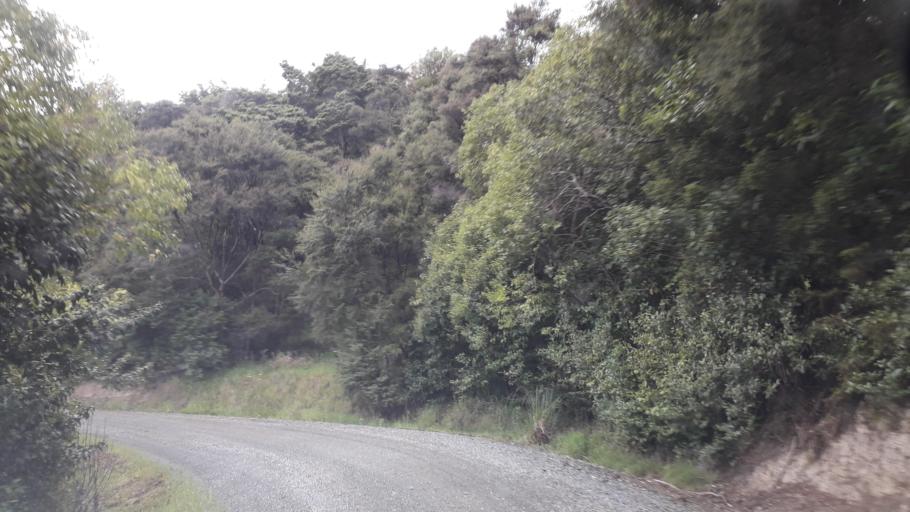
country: NZ
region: Northland
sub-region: Far North District
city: Waimate North
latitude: -35.3088
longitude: 173.5634
